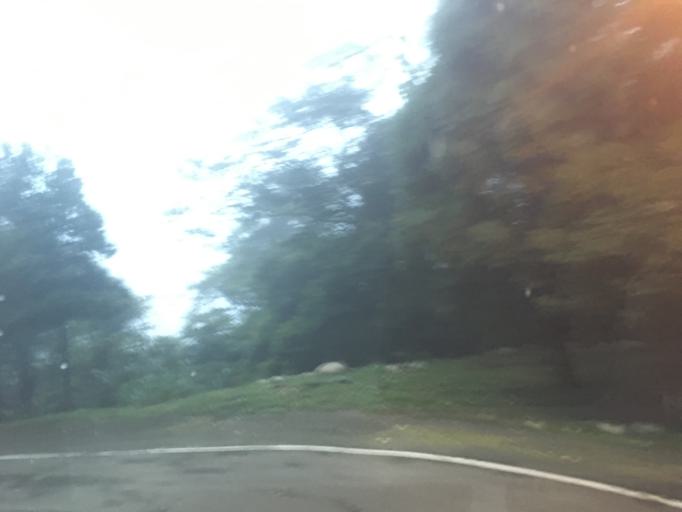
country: TW
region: Taiwan
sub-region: Miaoli
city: Miaoli
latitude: 24.4486
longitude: 120.7912
